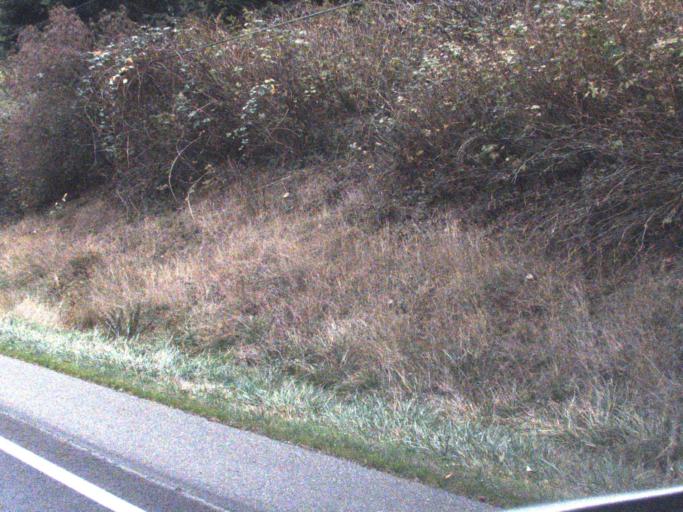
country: US
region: Washington
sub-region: Island County
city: Camano
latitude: 48.1024
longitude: -122.5754
